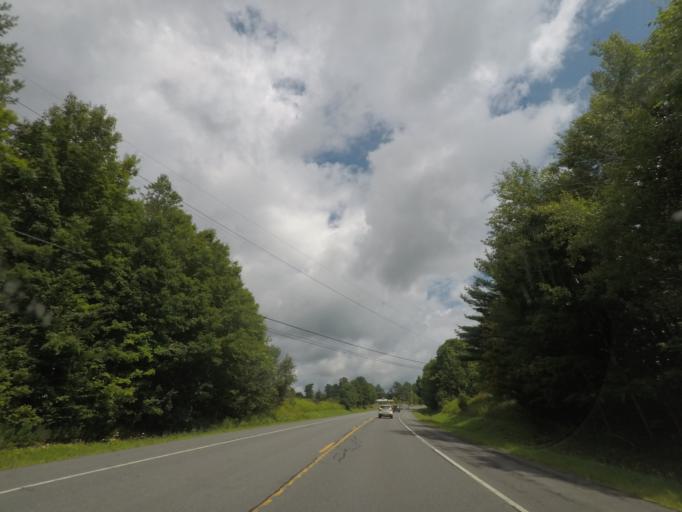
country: US
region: Massachusetts
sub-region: Berkshire County
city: Lanesborough
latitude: 42.5574
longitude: -73.3743
